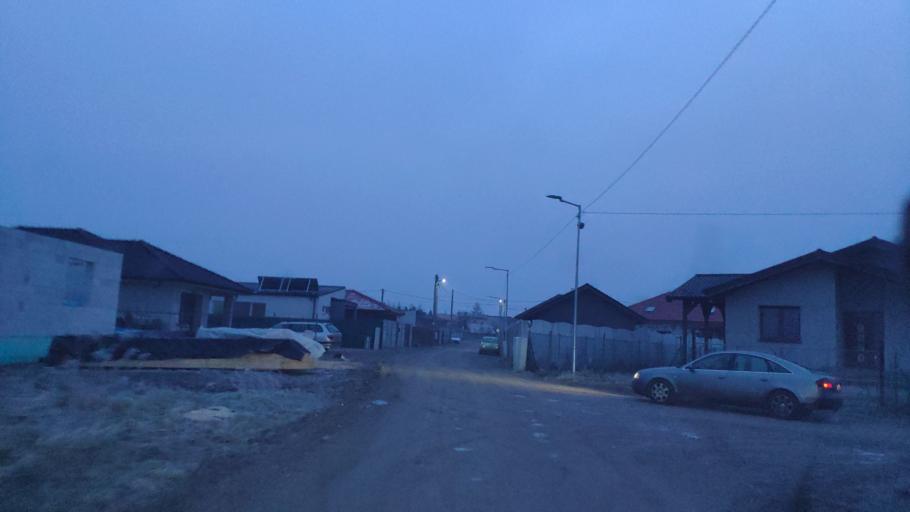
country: SK
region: Kosicky
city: Kosice
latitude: 48.6133
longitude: 21.3310
